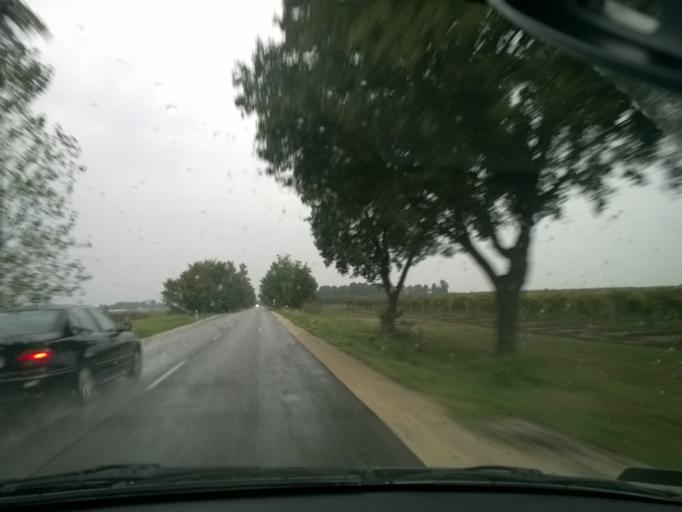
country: HU
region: Pest
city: Domsod
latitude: 47.0623
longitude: 19.0161
